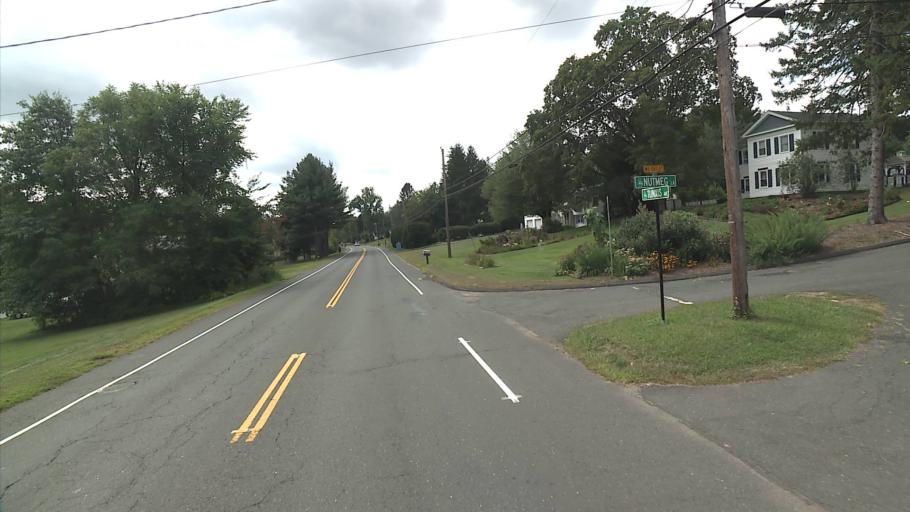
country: US
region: Connecticut
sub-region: Hartford County
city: Blue Hills
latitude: 41.8500
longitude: -72.7432
